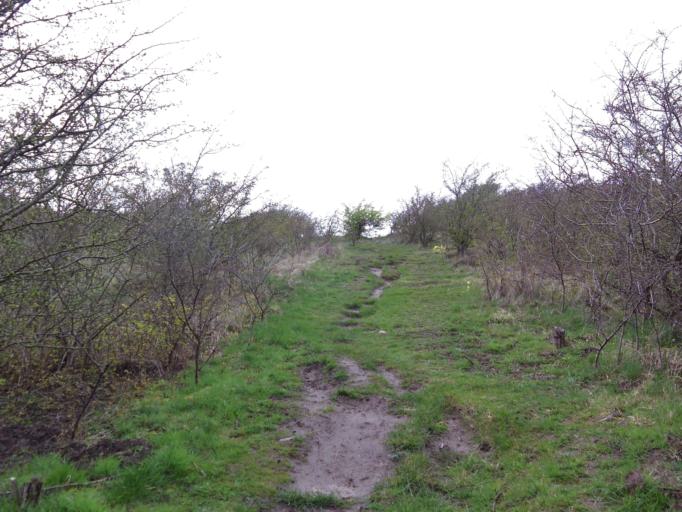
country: DE
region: Mecklenburg-Vorpommern
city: Hiddensee
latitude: 54.6035
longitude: 13.1305
